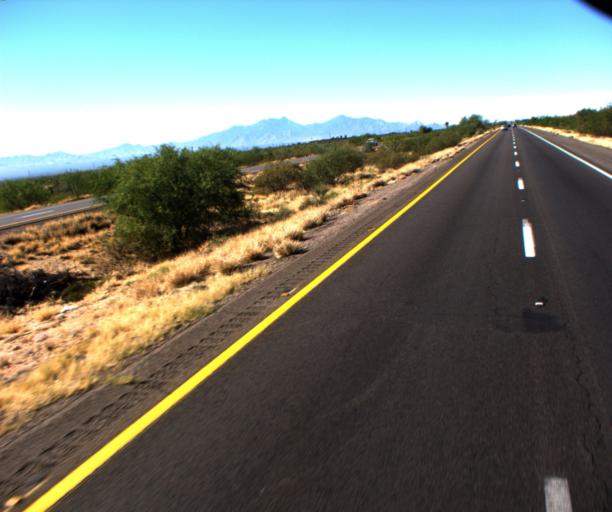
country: US
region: Arizona
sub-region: Pima County
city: Summit
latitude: 32.0183
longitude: -110.9926
